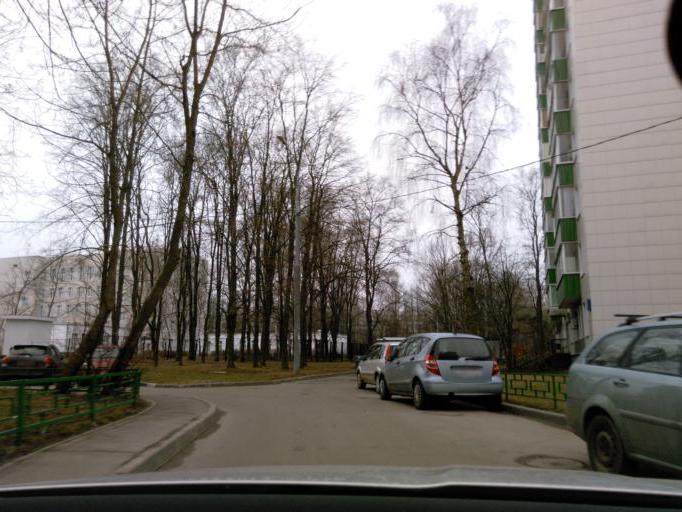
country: RU
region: Moskovskaya
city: Rzhavki
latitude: 55.9953
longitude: 37.2211
